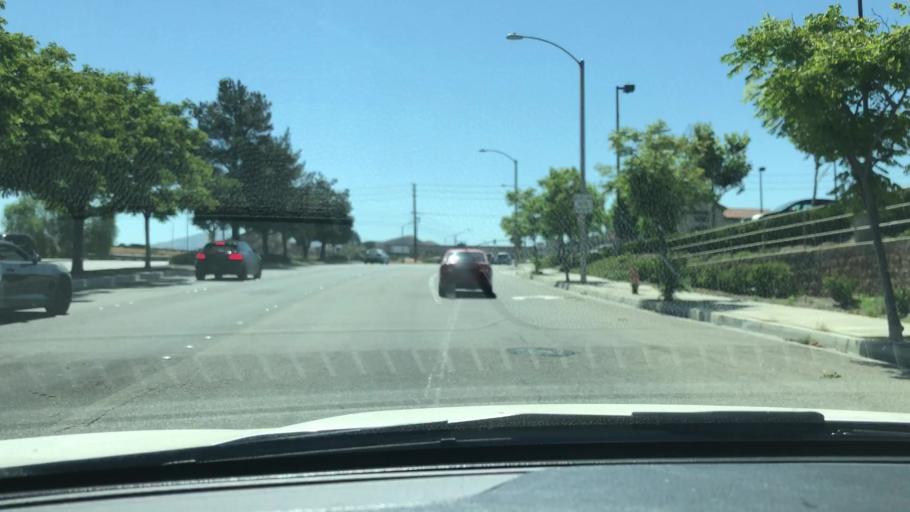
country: US
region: California
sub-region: Los Angeles County
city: Santa Clarita
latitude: 34.4067
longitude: -118.4670
